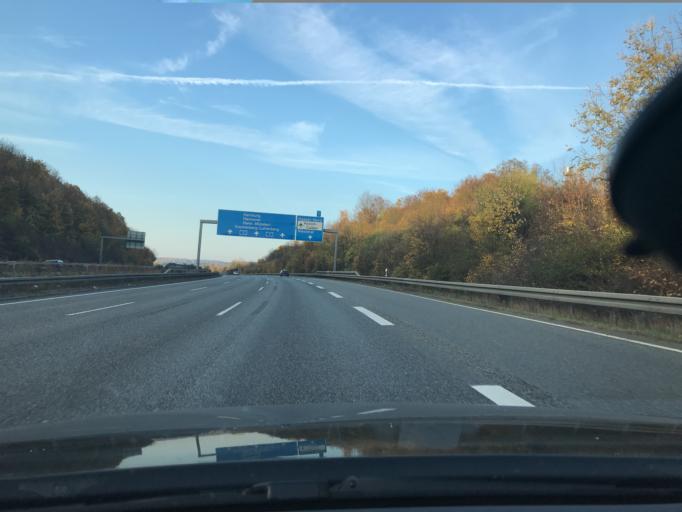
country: DE
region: Hesse
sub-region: Regierungsbezirk Kassel
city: Lohfelden
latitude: 51.2982
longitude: 9.5630
